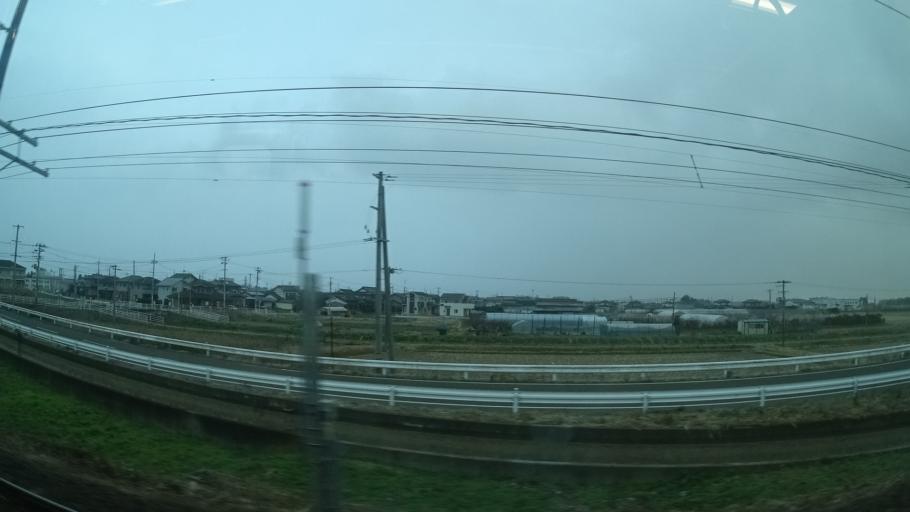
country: JP
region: Miyagi
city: Watari
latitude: 38.0660
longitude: 140.8549
